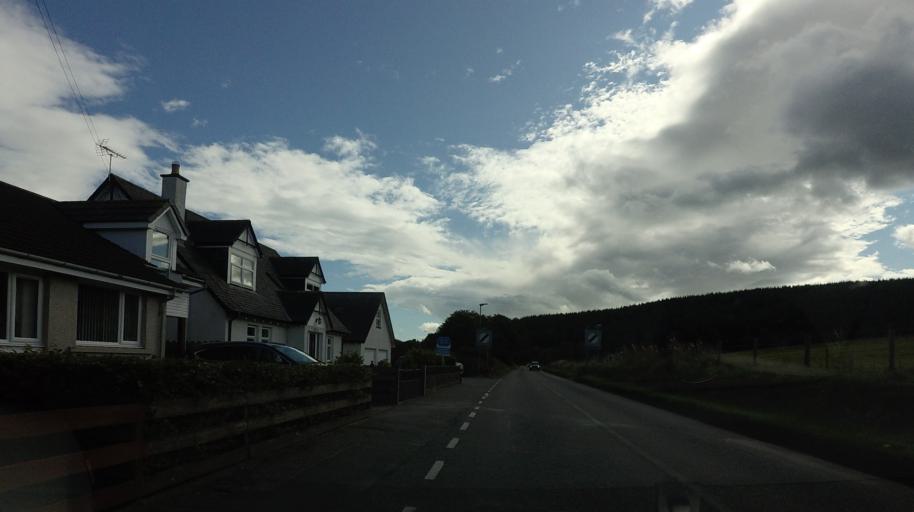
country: GB
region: Scotland
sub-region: Aberdeenshire
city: Torphins
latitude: 57.1269
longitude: -2.6783
